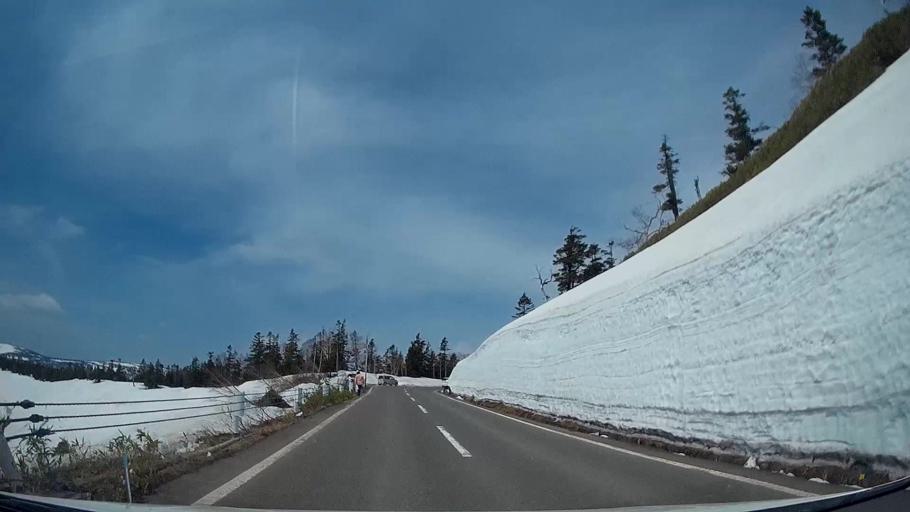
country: JP
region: Akita
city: Hanawa
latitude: 39.9512
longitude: 140.8917
